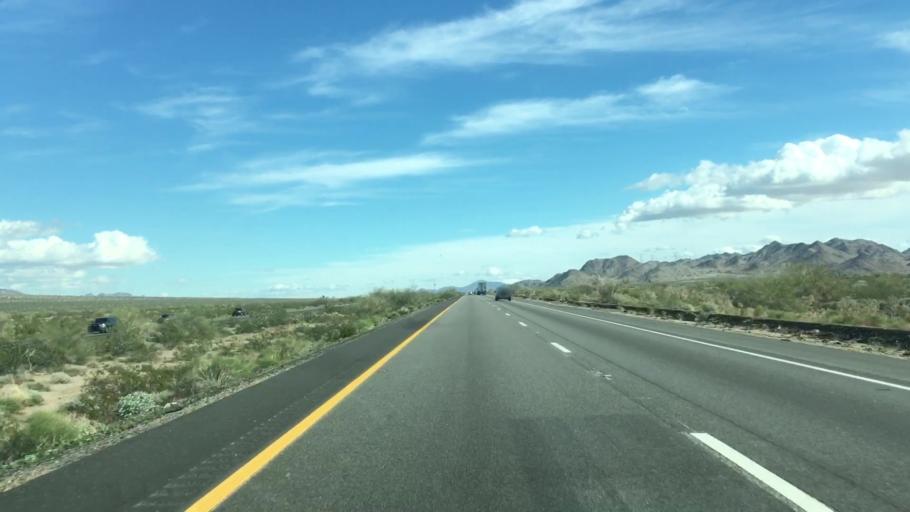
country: US
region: California
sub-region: Riverside County
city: Mecca
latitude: 33.6599
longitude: -115.7620
